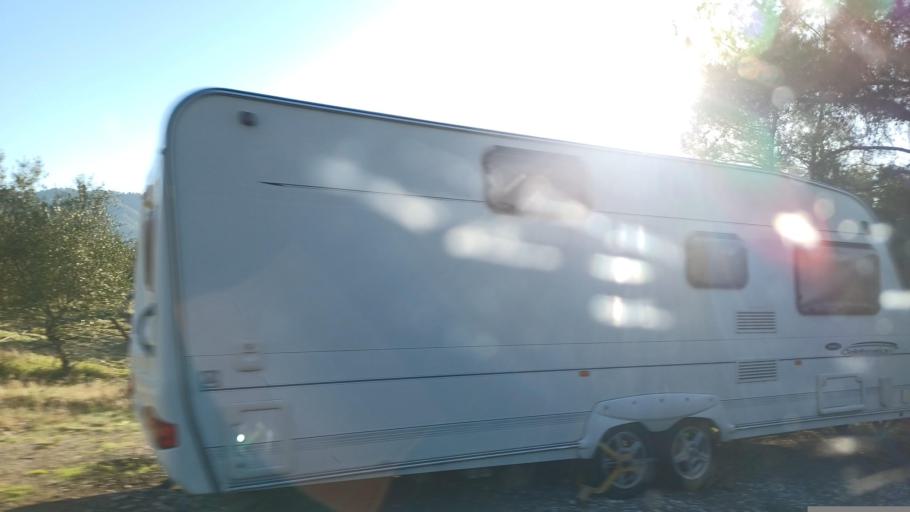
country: CY
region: Pafos
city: Mesogi
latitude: 34.9407
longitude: 32.5694
